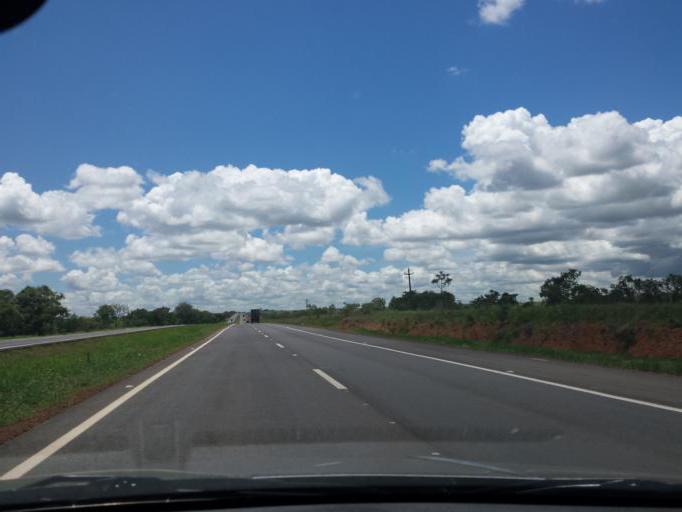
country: BR
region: Goias
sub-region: Cristalina
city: Cristalina
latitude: -16.6824
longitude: -47.7045
